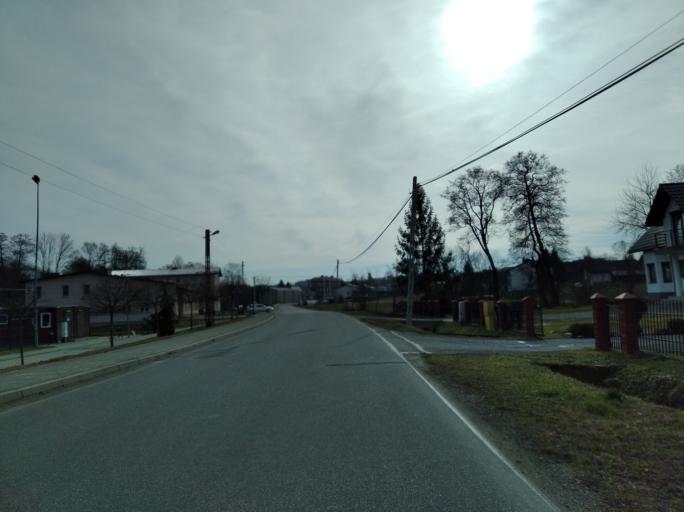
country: PL
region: Subcarpathian Voivodeship
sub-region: Powiat brzozowski
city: Orzechowka
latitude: 49.7324
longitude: 21.9438
